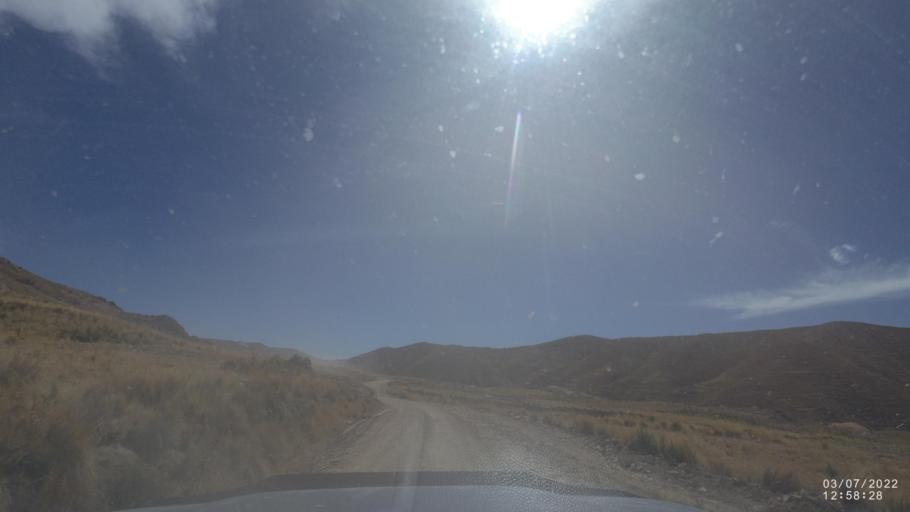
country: BO
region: Cochabamba
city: Sipe Sipe
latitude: -17.7212
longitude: -66.6806
